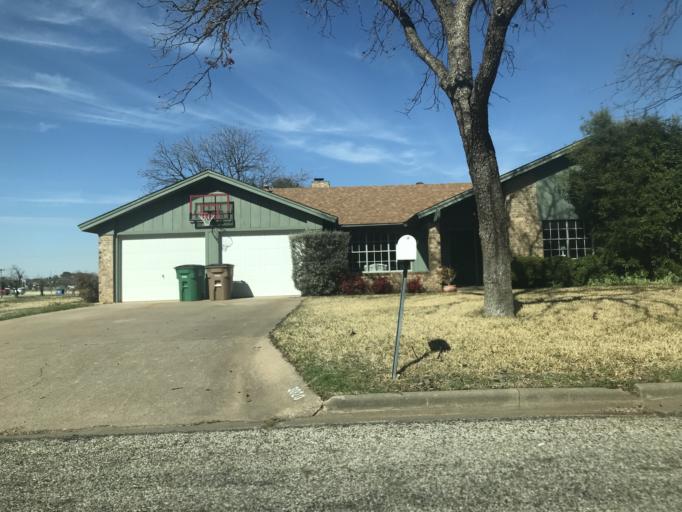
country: US
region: Texas
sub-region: Tom Green County
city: San Angelo
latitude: 31.4280
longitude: -100.4779
